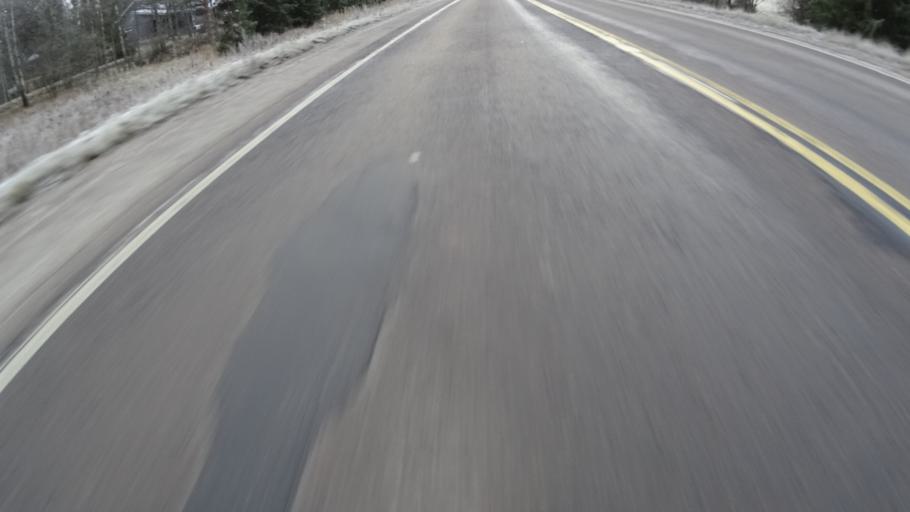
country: FI
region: Uusimaa
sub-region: Helsinki
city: Nurmijaervi
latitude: 60.4003
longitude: 24.7329
